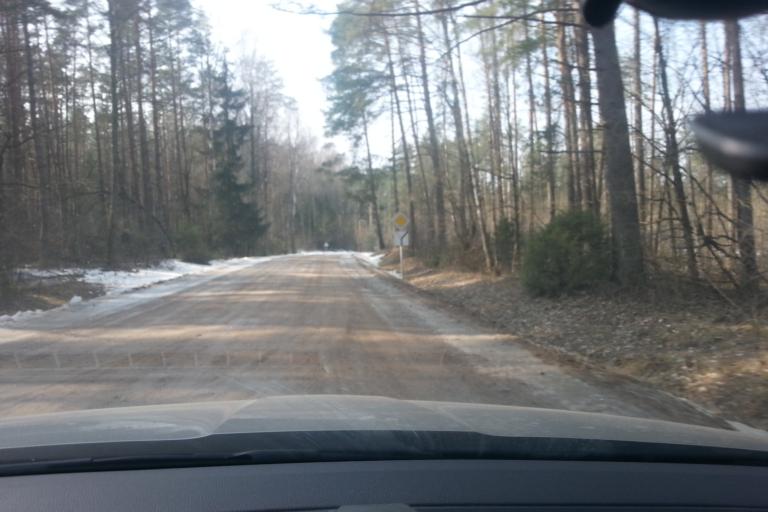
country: LT
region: Vilnius County
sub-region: Trakai
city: Rudiskes
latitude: 54.5113
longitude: 24.9332
